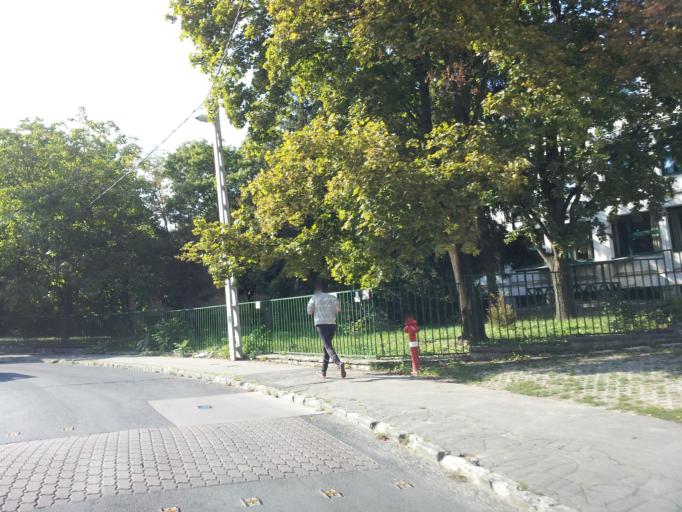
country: HU
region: Budapest
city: Budapest XII. keruelet
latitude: 47.5282
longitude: 18.9860
